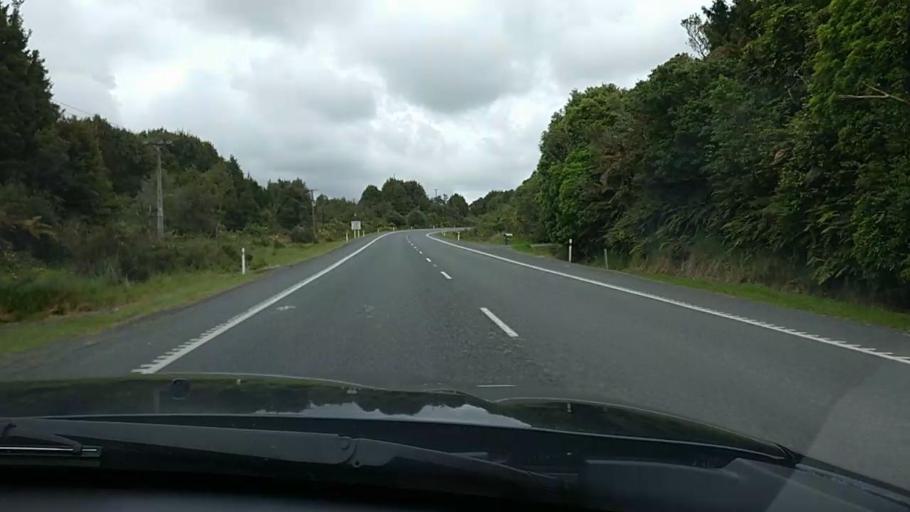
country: NZ
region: Bay of Plenty
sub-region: Rotorua District
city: Rotorua
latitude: -38.0719
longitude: 176.1254
